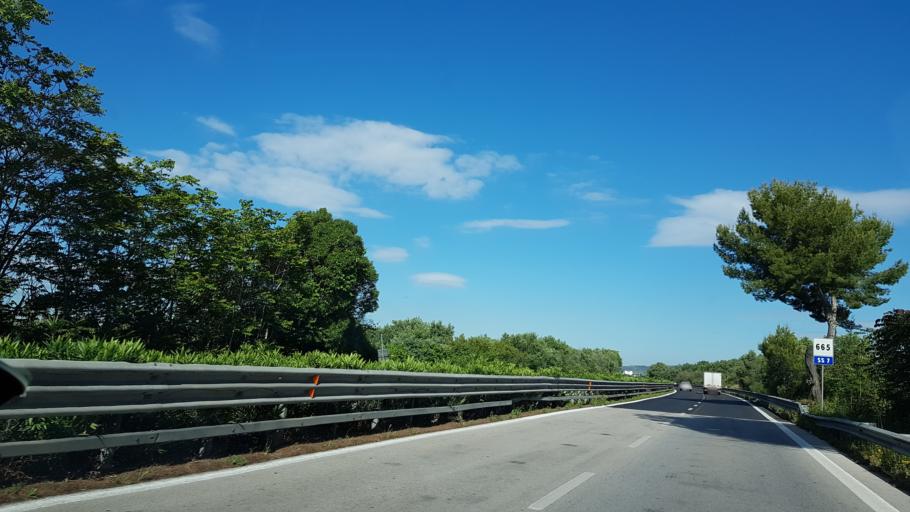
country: IT
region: Apulia
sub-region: Provincia di Taranto
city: Grottaglie
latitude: 40.5298
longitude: 17.4085
